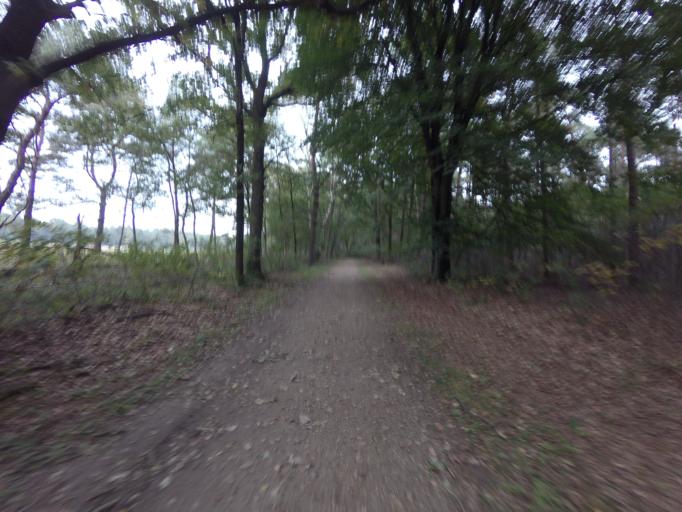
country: NL
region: North Holland
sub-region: Gemeente Hilversum
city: Hilversum
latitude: 52.2000
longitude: 5.1994
